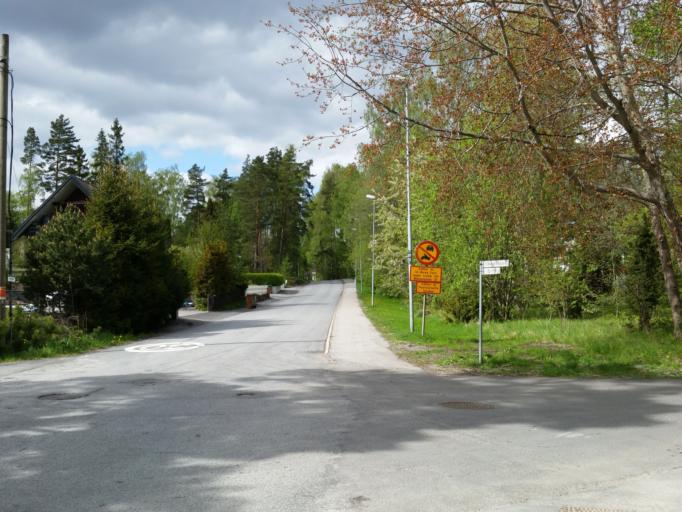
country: SE
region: Stockholm
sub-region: Sollentuna Kommun
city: Sollentuna
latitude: 59.4576
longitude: 17.9497
